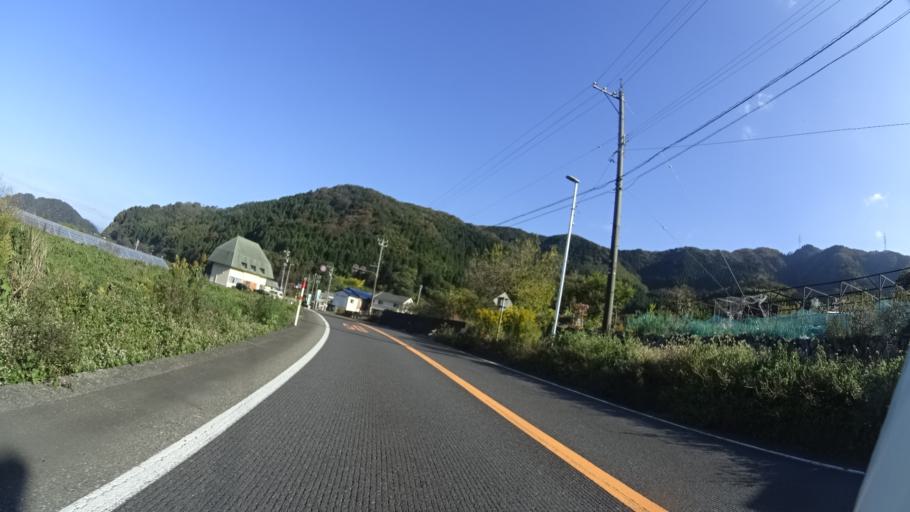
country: JP
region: Fukui
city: Tsuruga
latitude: 35.7225
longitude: 136.0991
